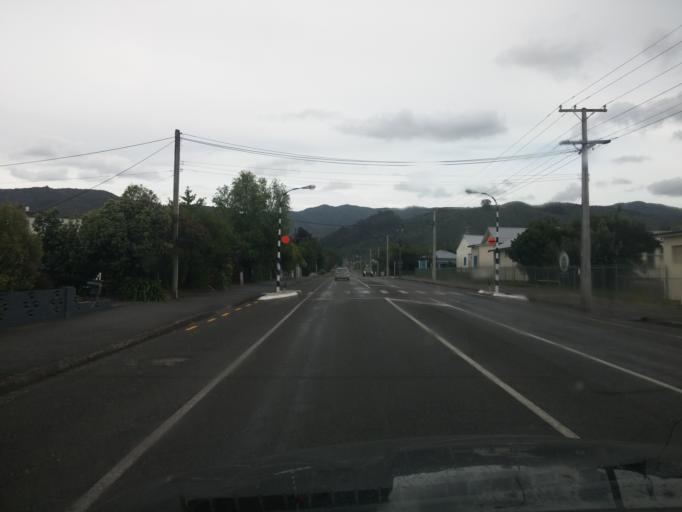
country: NZ
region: Wellington
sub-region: Upper Hutt City
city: Upper Hutt
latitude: -41.1195
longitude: 175.3271
